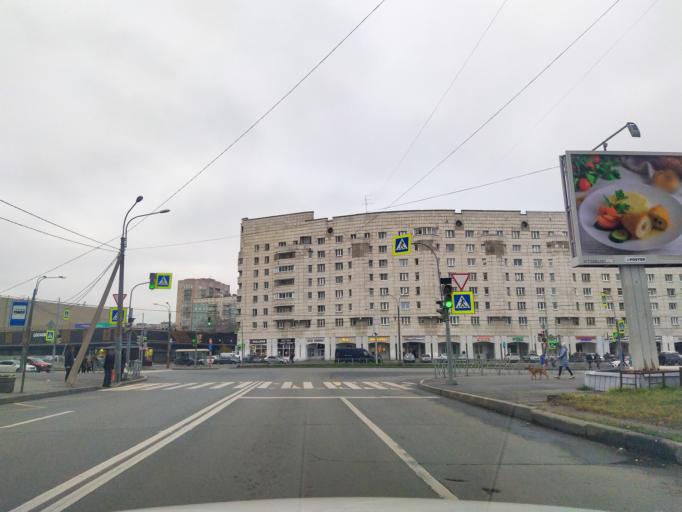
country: RU
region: St.-Petersburg
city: Sosnovka
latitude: 60.0355
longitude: 30.3427
